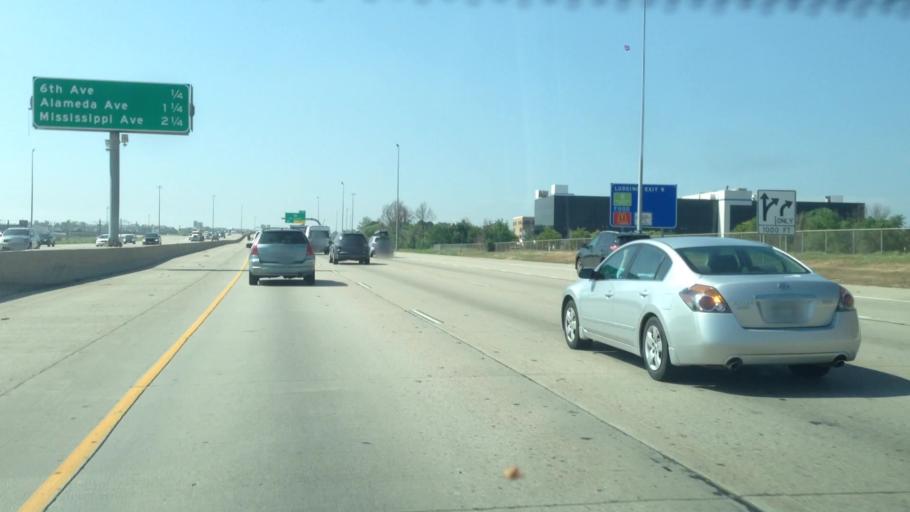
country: US
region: Colorado
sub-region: Adams County
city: Aurora
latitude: 39.7322
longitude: -104.8254
